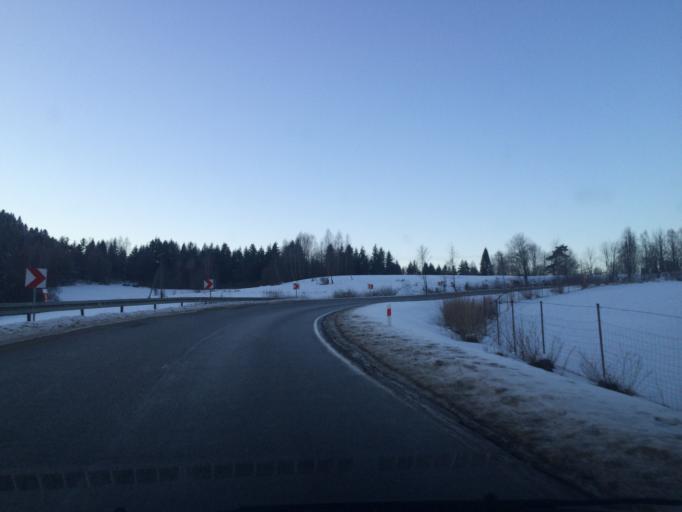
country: PL
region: Subcarpathian Voivodeship
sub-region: Powiat bieszczadzki
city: Czarna
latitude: 49.3490
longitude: 22.6822
